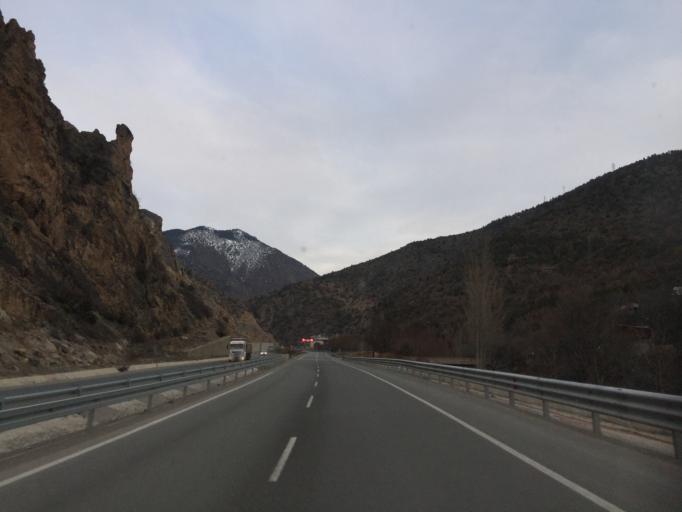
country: TR
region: Gumushane
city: Gumushkhane
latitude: 40.5214
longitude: 39.4034
